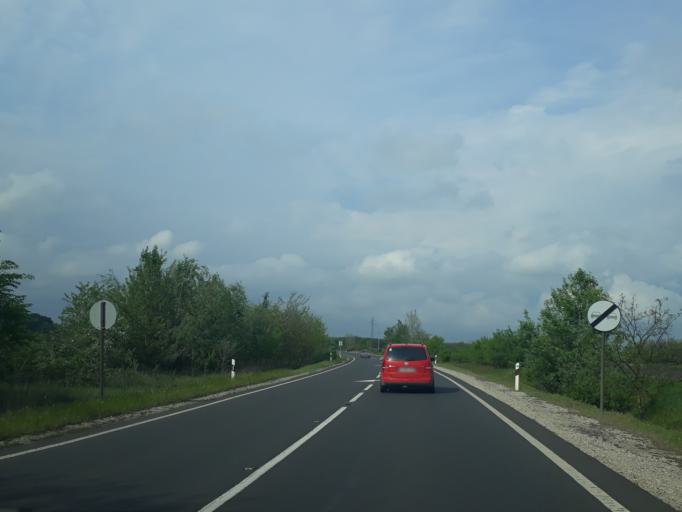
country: HU
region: Szabolcs-Szatmar-Bereg
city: Nyirbogdany
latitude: 48.0604
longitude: 21.9259
